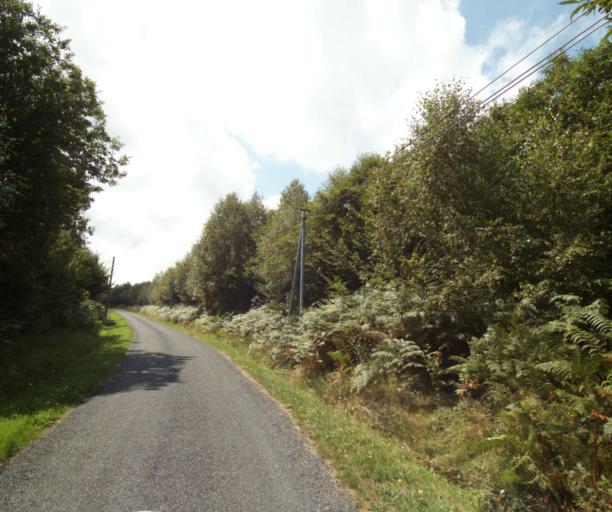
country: FR
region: Limousin
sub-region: Departement de la Correze
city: Sainte-Fortunade
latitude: 45.2051
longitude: 1.8124
